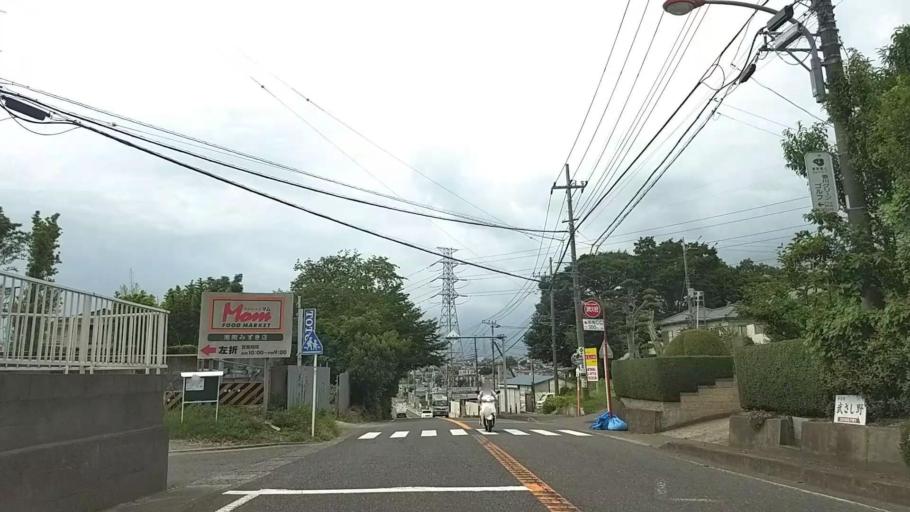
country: JP
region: Kanagawa
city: Chigasaki
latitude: 35.3672
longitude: 139.4043
